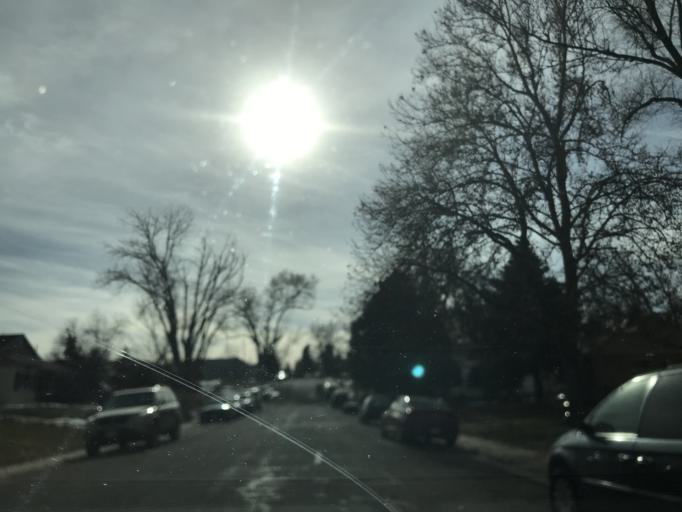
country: US
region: Colorado
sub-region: Arapahoe County
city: Littleton
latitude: 39.6070
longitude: -105.0151
